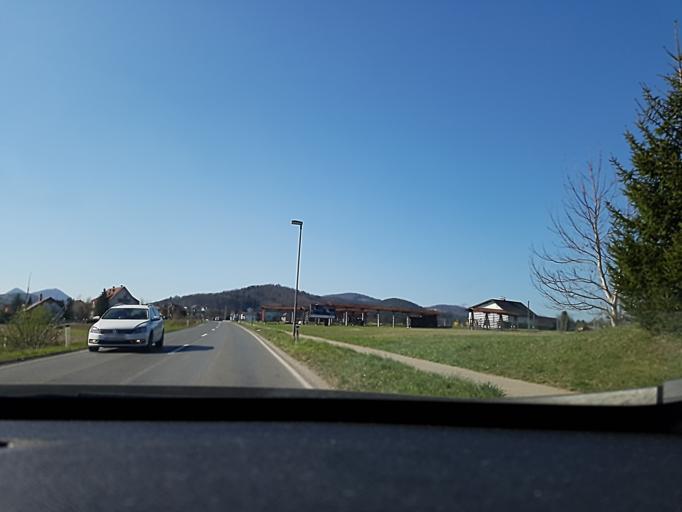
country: SI
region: Trzin
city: Trzin
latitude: 46.0991
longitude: 14.5556
